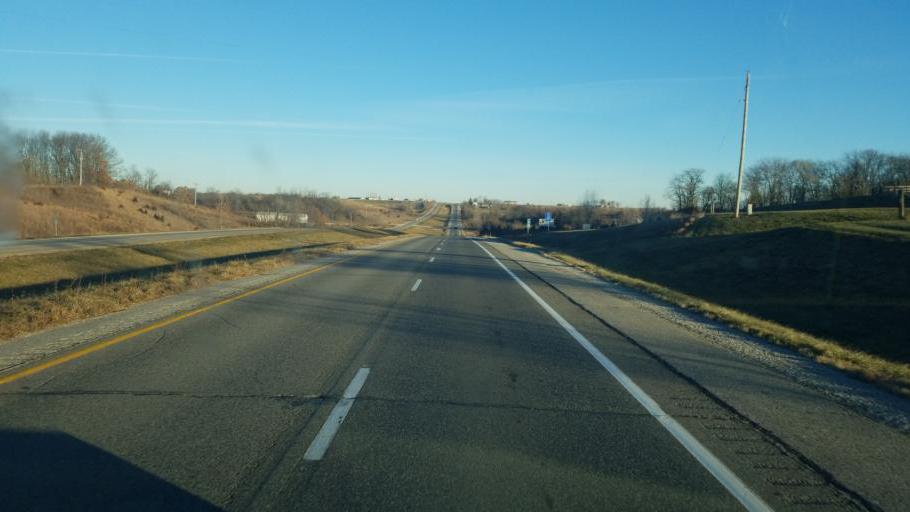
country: US
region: Iowa
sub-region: Wapello County
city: Eddyville
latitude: 41.2177
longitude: -92.6404
